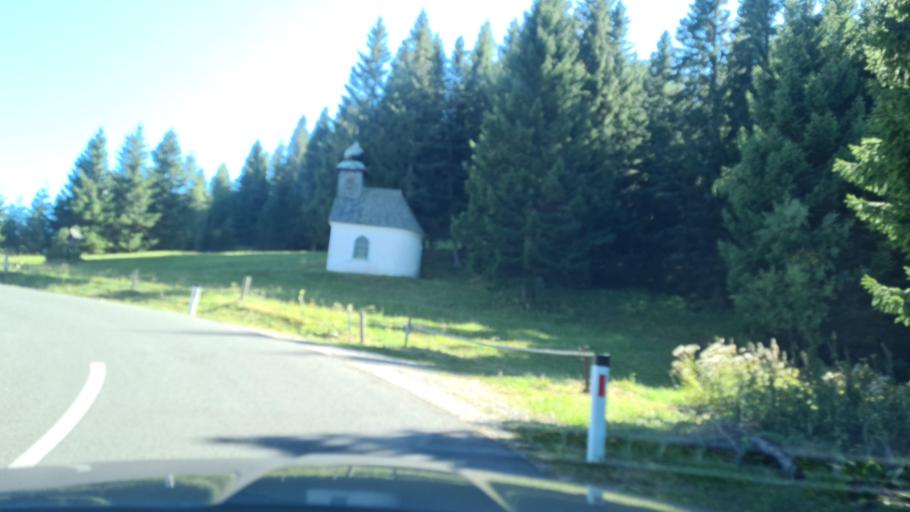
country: AT
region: Styria
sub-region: Politischer Bezirk Weiz
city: Gasen
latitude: 47.3450
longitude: 15.5518
